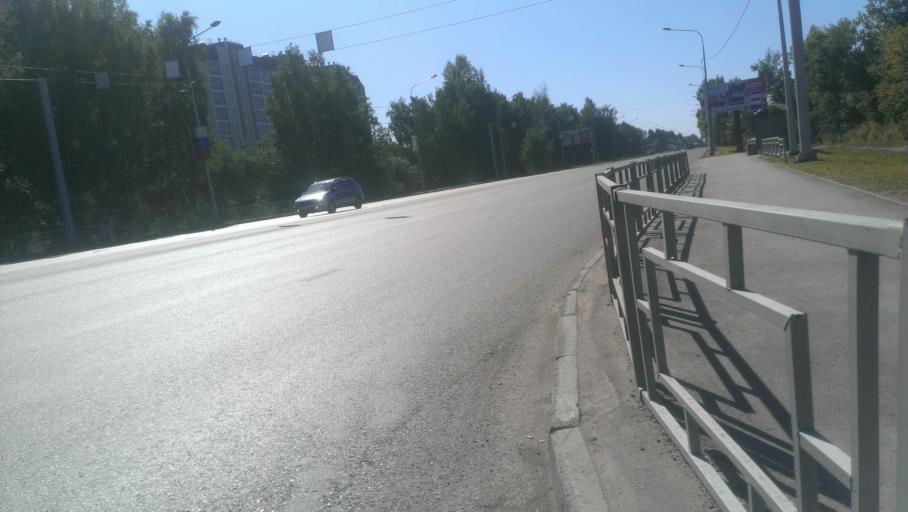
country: RU
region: Altai Krai
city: Novosilikatnyy
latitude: 53.3467
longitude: 83.6497
